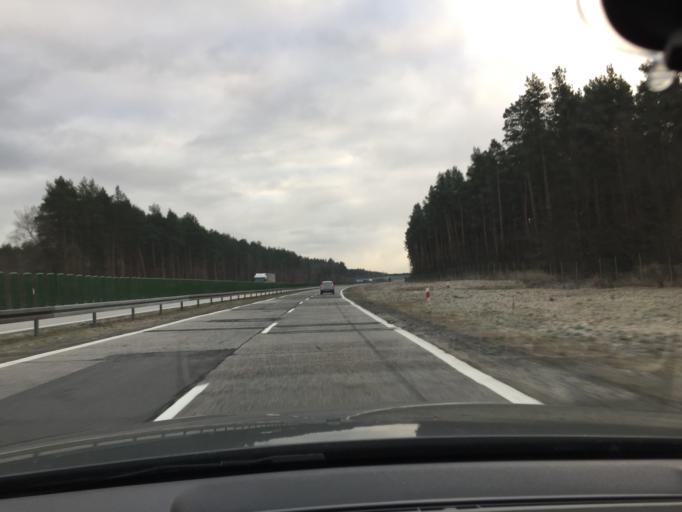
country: PL
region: Lubusz
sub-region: Powiat zarski
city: Lipinki Luzyckie
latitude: 51.6057
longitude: 14.9844
